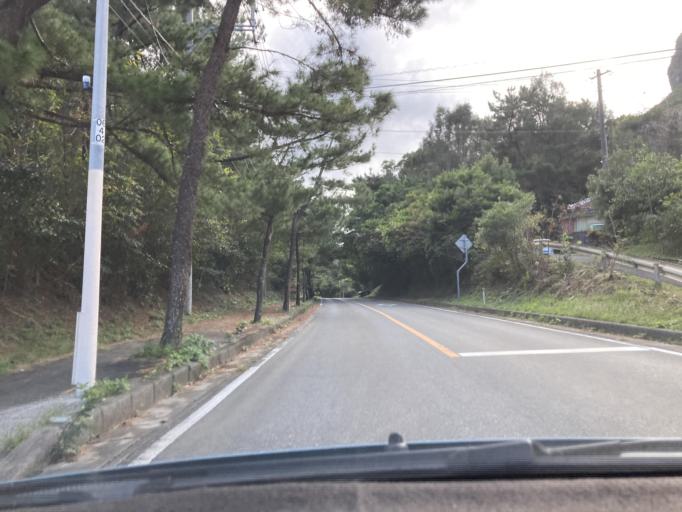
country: JP
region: Okinawa
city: Nago
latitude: 26.8564
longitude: 128.2603
